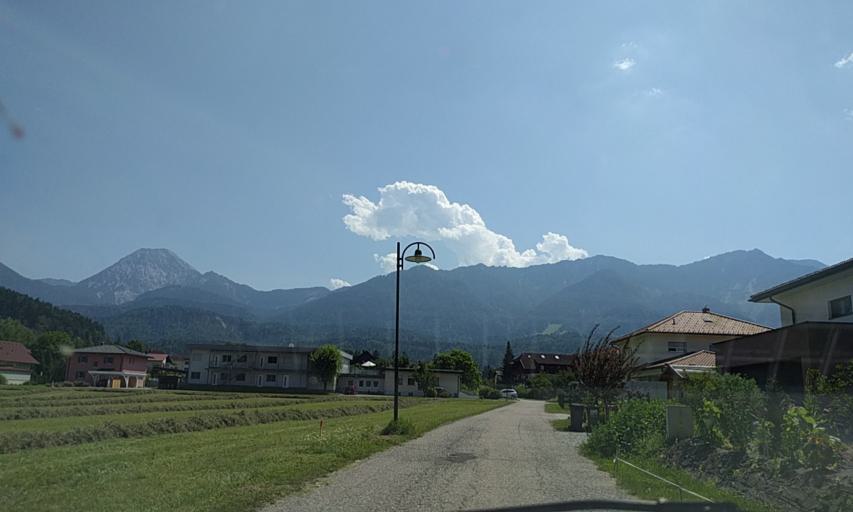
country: AT
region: Carinthia
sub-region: Politischer Bezirk Villach Land
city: Finkenstein am Faaker See
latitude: 46.5689
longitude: 13.9101
